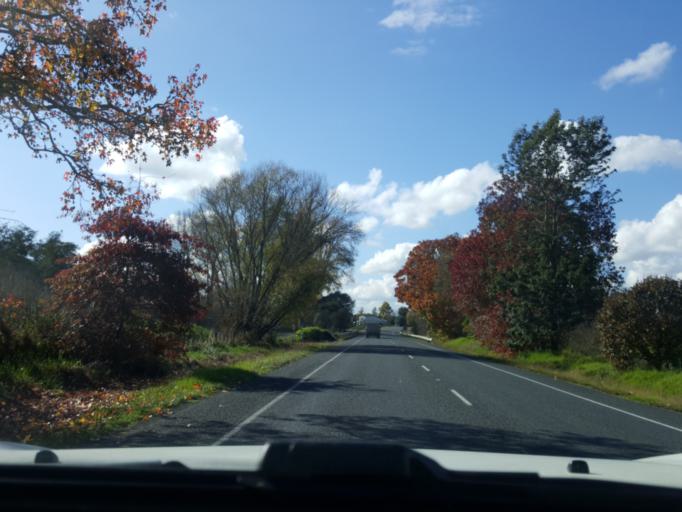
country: NZ
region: Waikato
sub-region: Waikato District
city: Ngaruawahia
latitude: -37.6294
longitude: 175.1788
